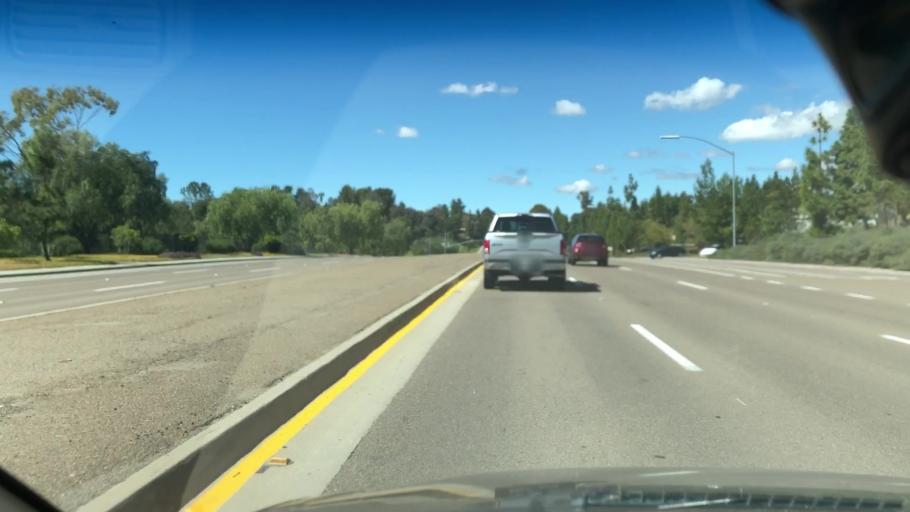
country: US
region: California
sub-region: San Diego County
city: Poway
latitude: 32.9894
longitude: -117.0697
